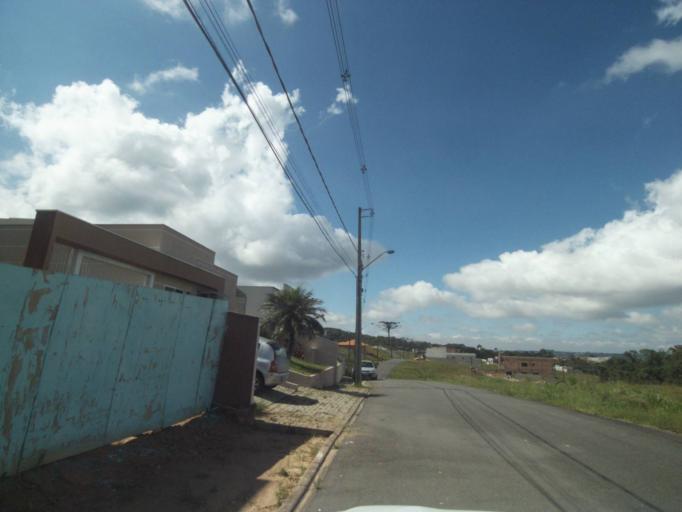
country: BR
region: Parana
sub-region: Colombo
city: Colombo
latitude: -25.3103
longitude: -49.2341
